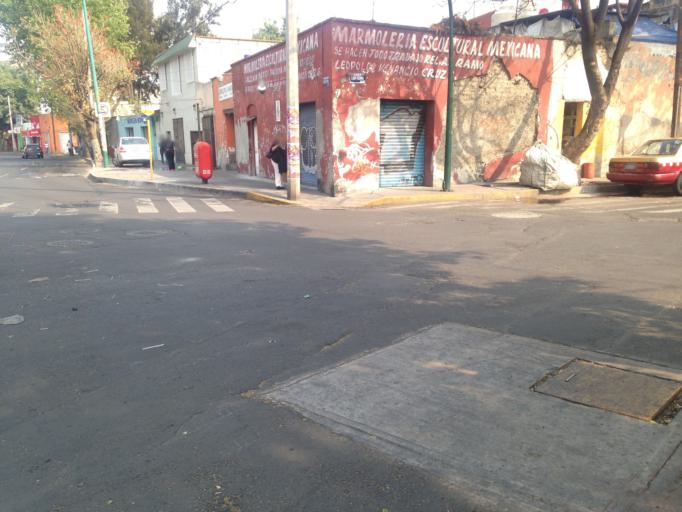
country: MX
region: Mexico City
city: Miguel Hidalgo
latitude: 19.4582
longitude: -99.2017
